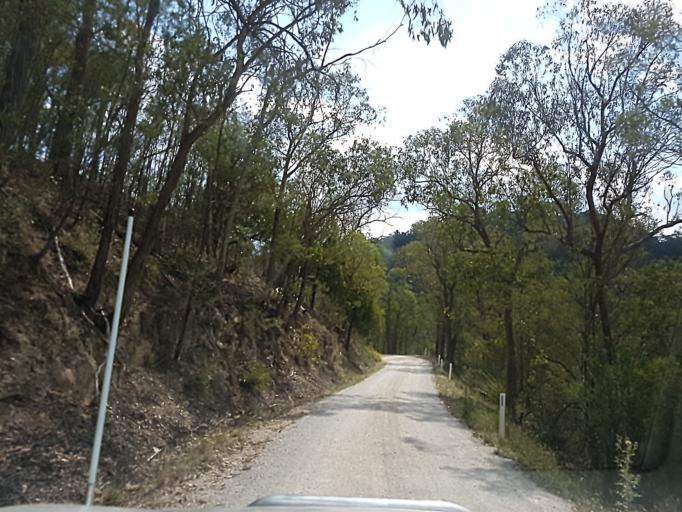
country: AU
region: Victoria
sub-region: East Gippsland
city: Lakes Entrance
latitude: -37.4892
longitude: 148.2345
